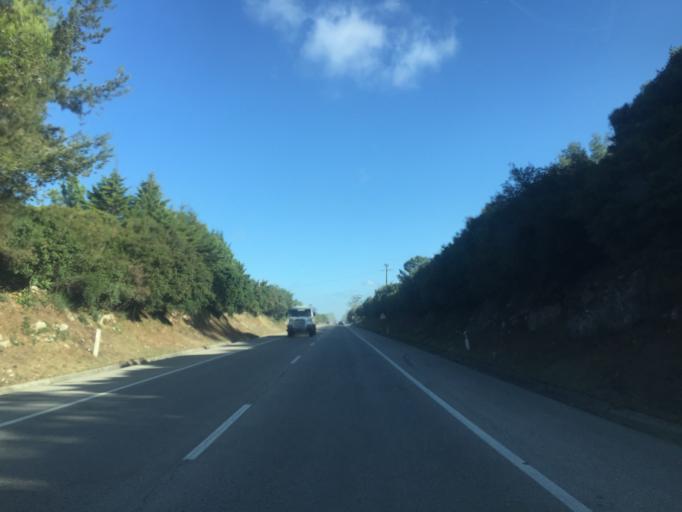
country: PT
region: Leiria
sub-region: Alcobaca
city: Turquel
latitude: 39.4517
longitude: -8.9492
